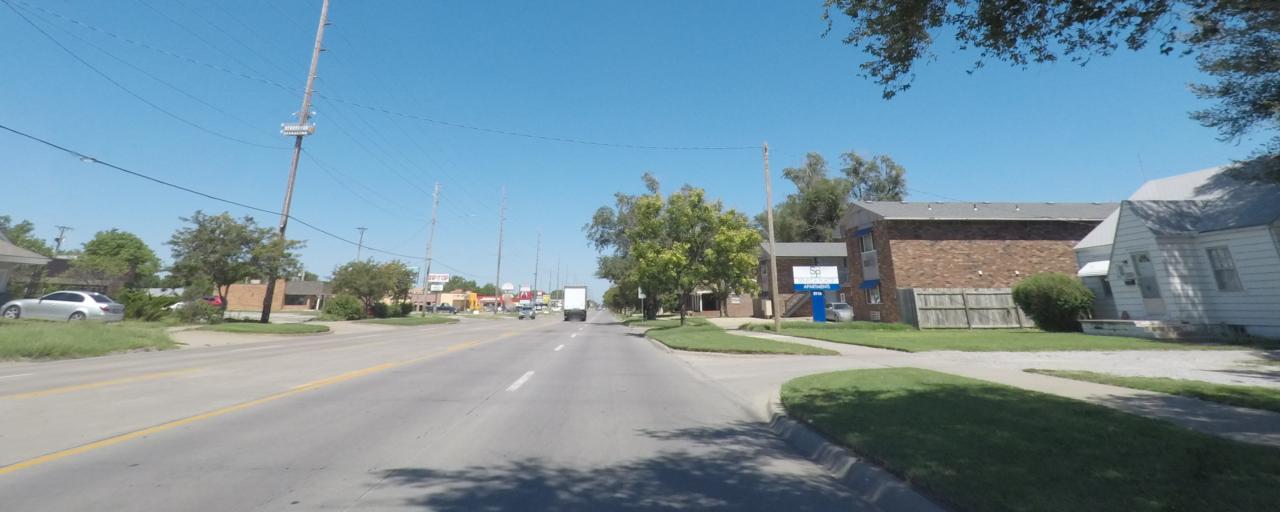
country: US
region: Kansas
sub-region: Sedgwick County
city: Wichita
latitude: 37.6557
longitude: -97.3527
